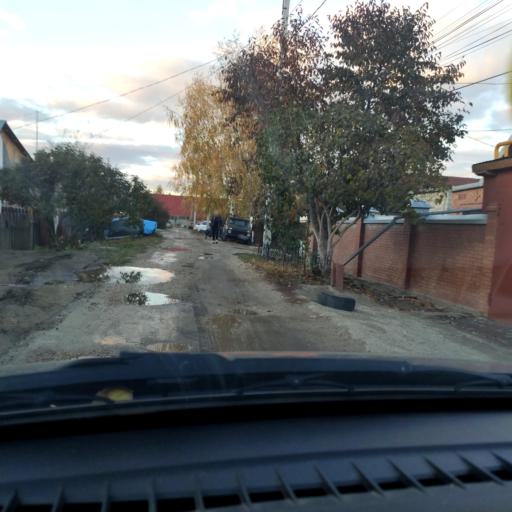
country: RU
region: Samara
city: Tol'yatti
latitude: 53.5393
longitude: 49.4219
